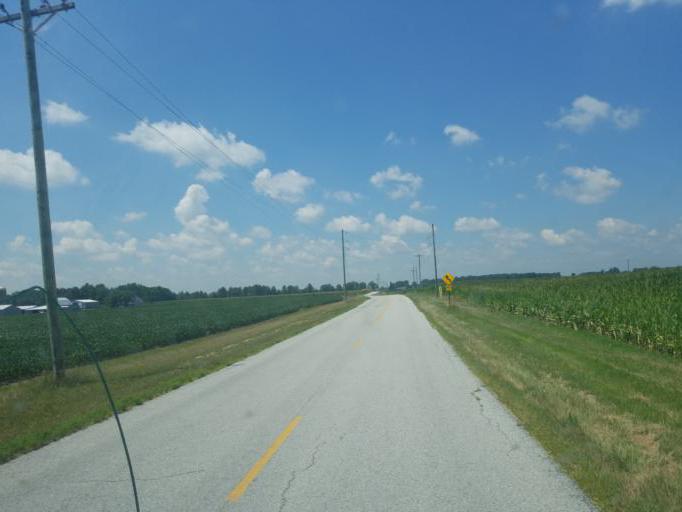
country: US
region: Ohio
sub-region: Allen County
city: Spencerville
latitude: 40.6776
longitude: -84.4532
